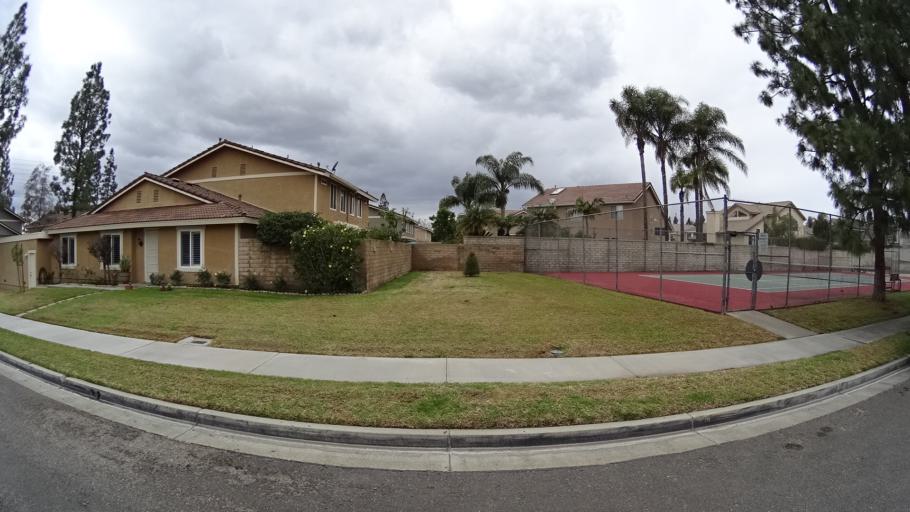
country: US
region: California
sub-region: Orange County
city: Yorba Linda
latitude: 33.8683
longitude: -117.8238
